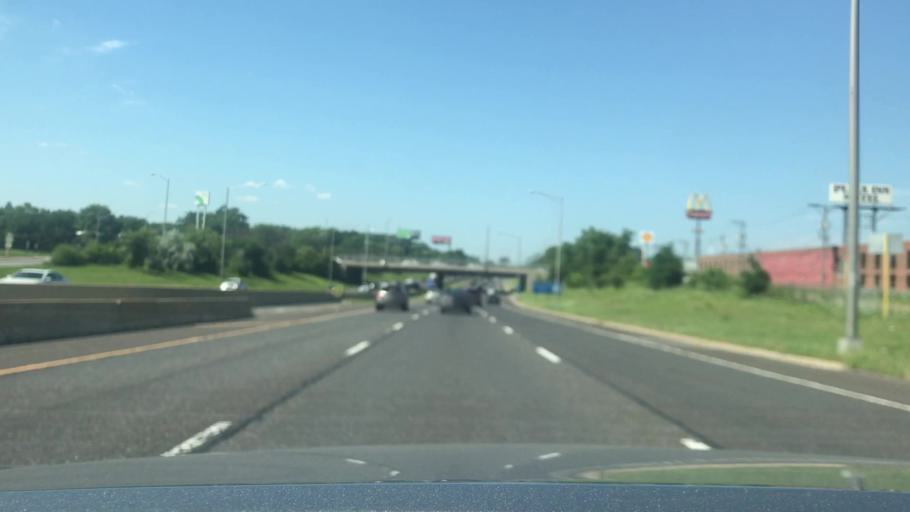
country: US
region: Illinois
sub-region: Cook County
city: Calumet Park
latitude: 41.6607
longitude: -87.6625
